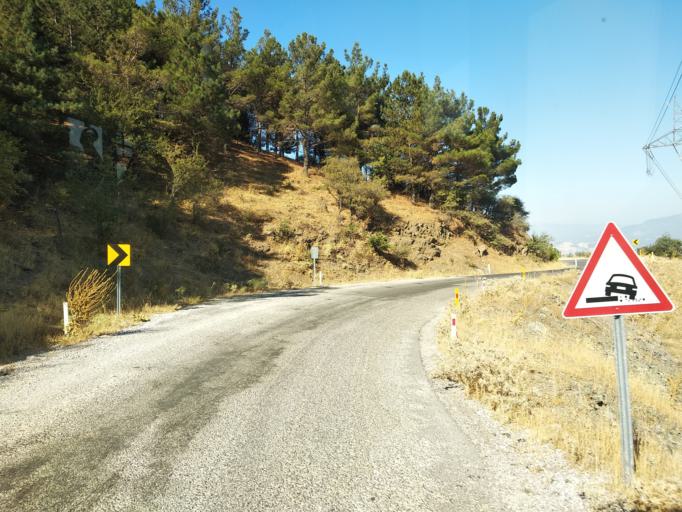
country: TR
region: Izmir
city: Gaziemir
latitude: 38.3157
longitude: 27.0087
